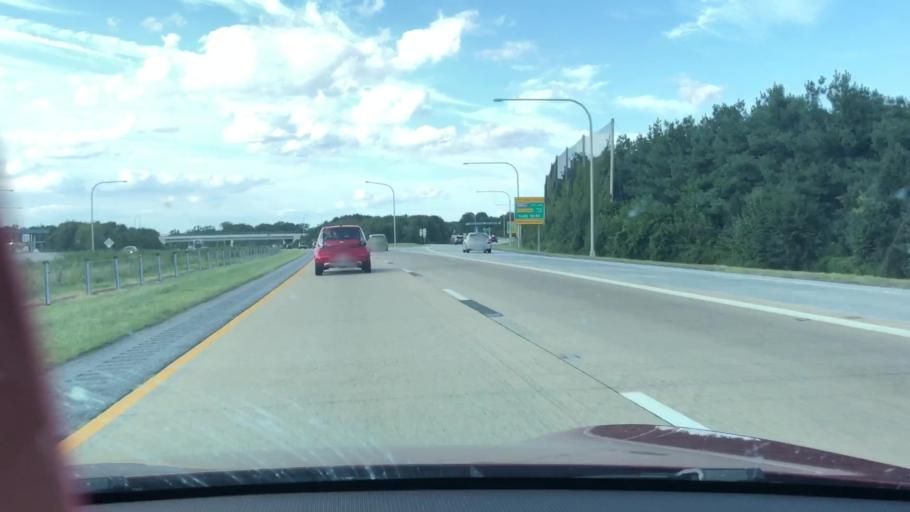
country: US
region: Delaware
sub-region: New Castle County
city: Middletown
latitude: 39.4964
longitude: -75.6469
